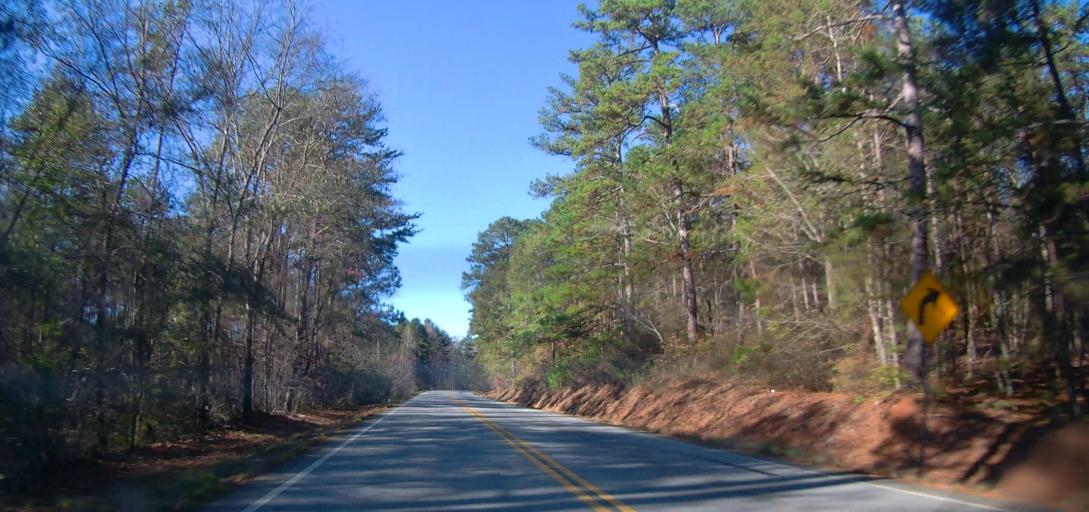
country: US
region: Georgia
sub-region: Hall County
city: Lula
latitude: 34.4213
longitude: -83.7092
